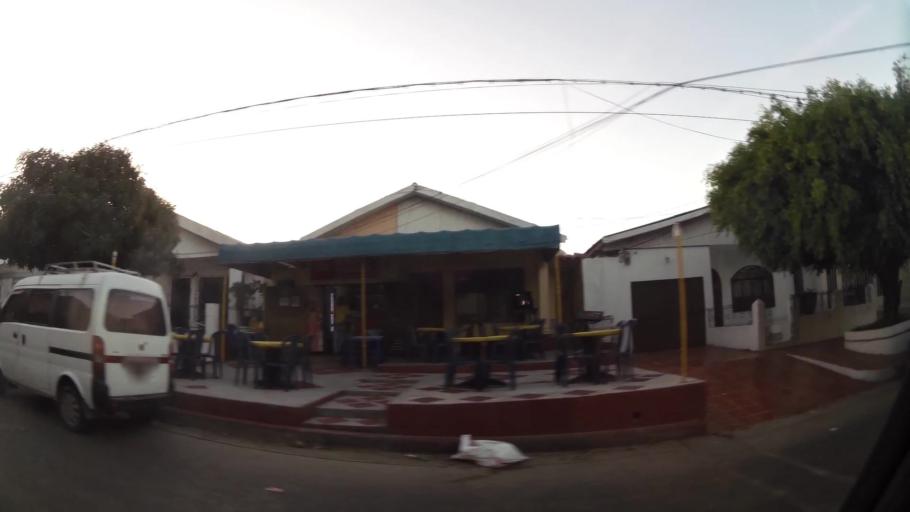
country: CO
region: Atlantico
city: Barranquilla
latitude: 10.9790
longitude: -74.8055
